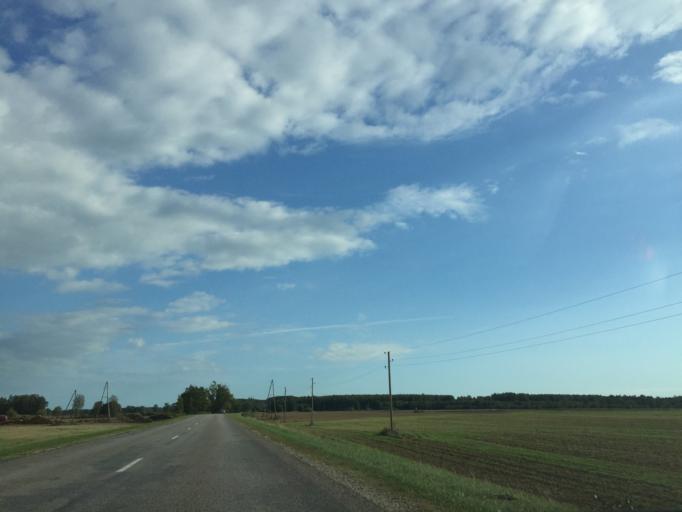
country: LV
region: Limbazu Rajons
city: Limbazi
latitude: 57.5080
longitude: 24.5063
